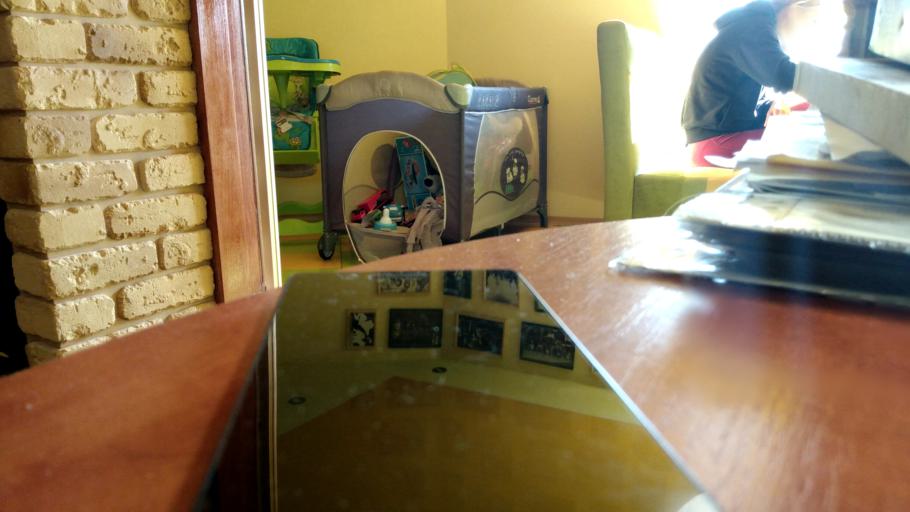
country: RU
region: Penza
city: Serdobsk
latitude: 52.3762
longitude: 44.3444
